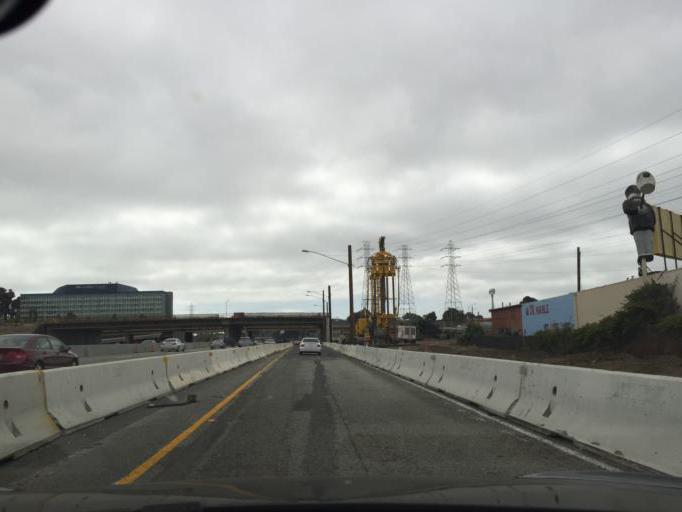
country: US
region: California
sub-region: San Mateo County
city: Burlingame
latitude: 37.5912
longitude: -122.3633
